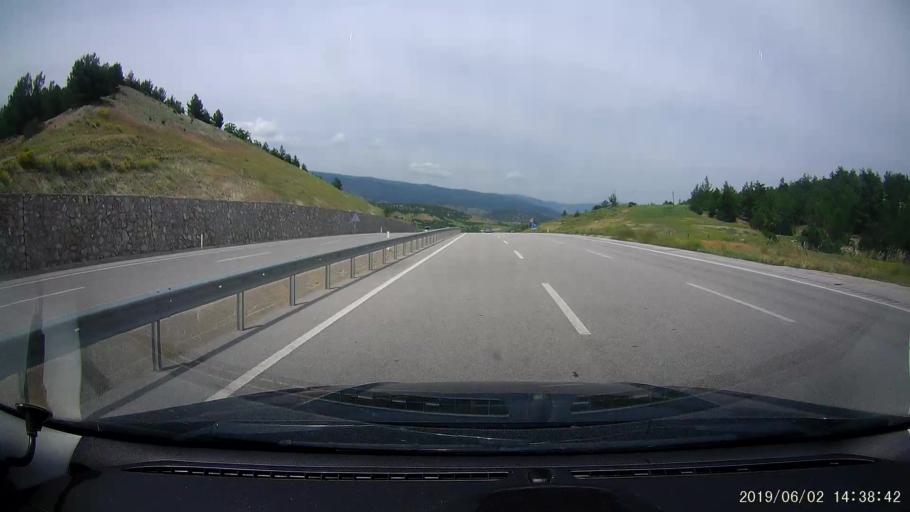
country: TR
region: Corum
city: Hacihamza
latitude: 41.0591
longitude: 34.2865
